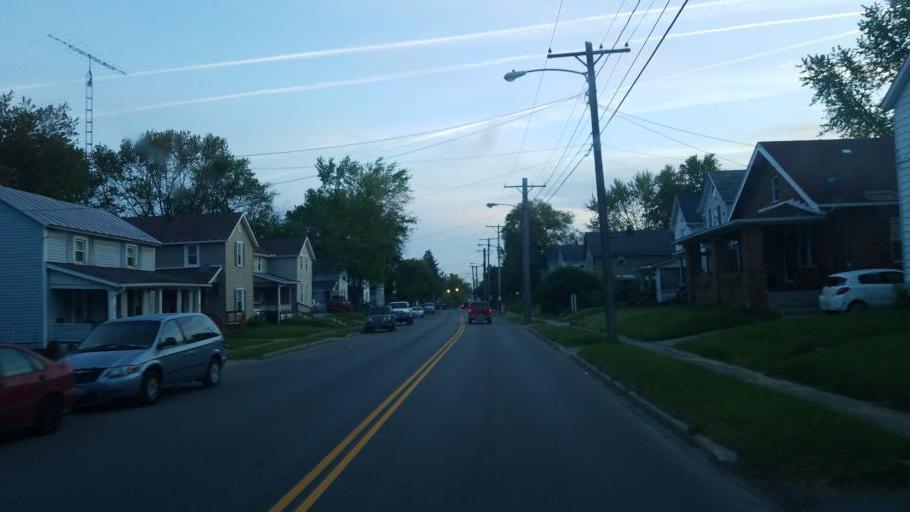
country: US
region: Ohio
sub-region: Richland County
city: Mansfield
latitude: 40.7680
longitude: -82.5065
